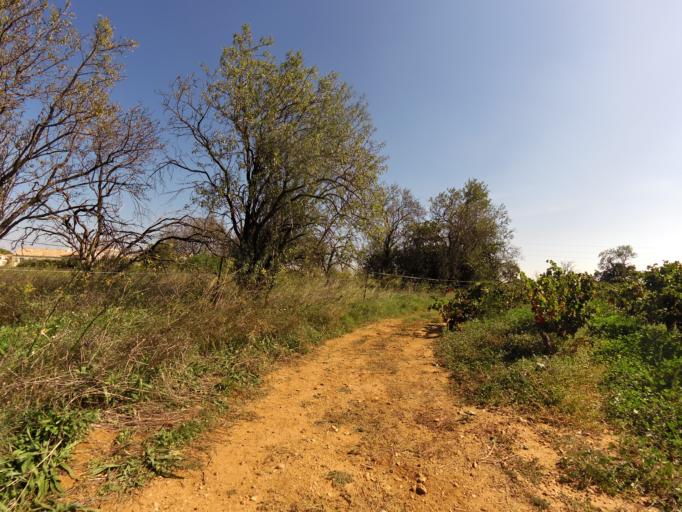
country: FR
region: Languedoc-Roussillon
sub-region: Departement du Gard
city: Gallargues-le-Montueux
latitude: 43.7227
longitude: 4.1601
